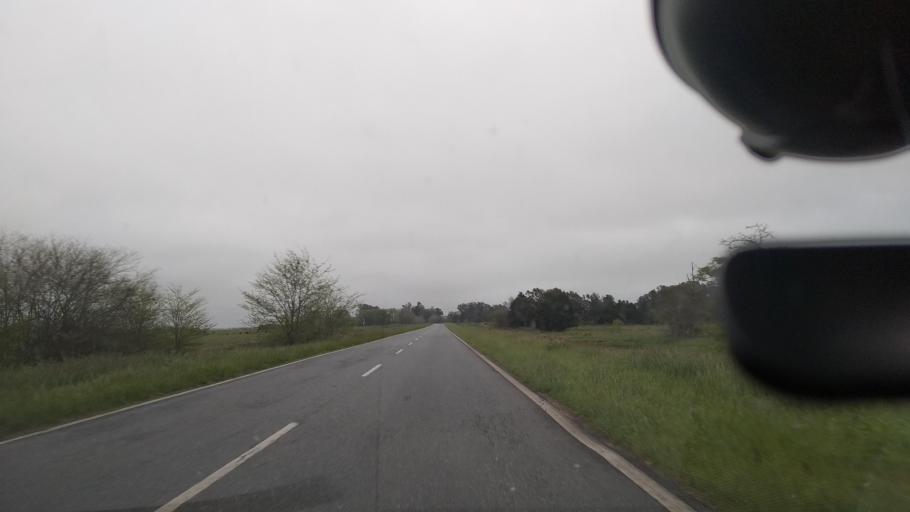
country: AR
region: Buenos Aires
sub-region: Partido de Magdalena
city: Magdalena
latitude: -35.2667
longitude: -57.6144
